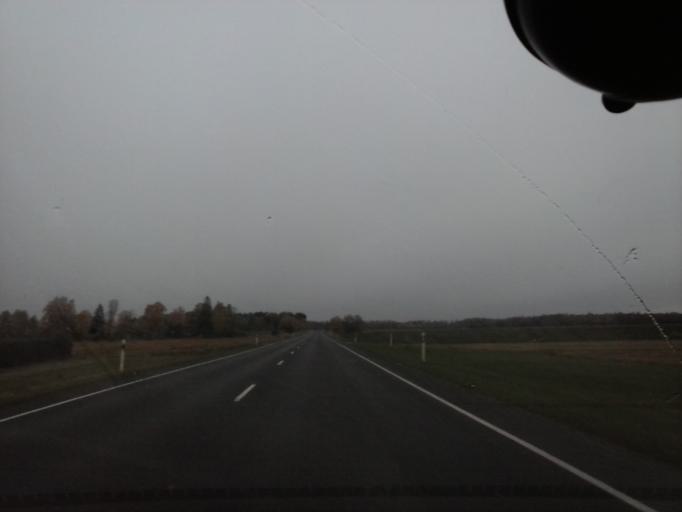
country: EE
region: Viljandimaa
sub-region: Vohma linn
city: Vohma
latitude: 58.7026
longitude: 25.6228
